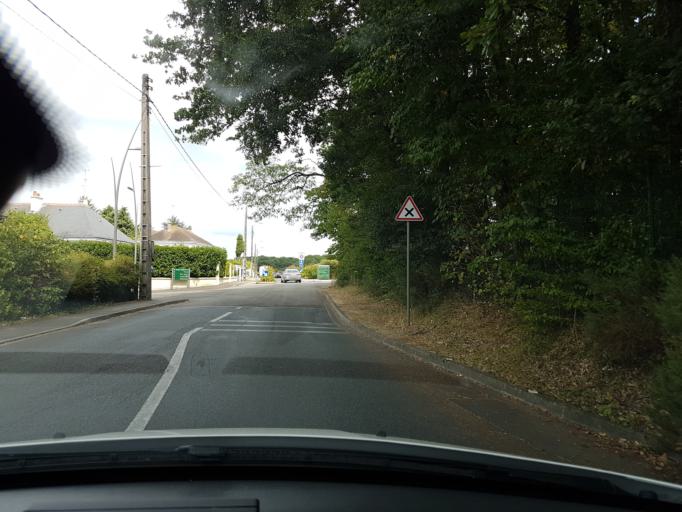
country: FR
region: Centre
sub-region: Departement d'Indre-et-Loire
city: Chambray-les-Tours
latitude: 47.3306
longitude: 0.7089
